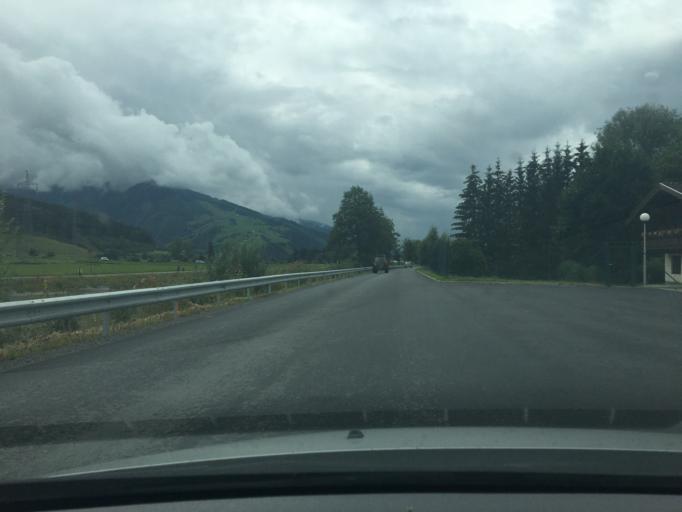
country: AT
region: Salzburg
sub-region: Politischer Bezirk Zell am See
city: Kaprun
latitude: 47.2823
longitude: 12.7892
